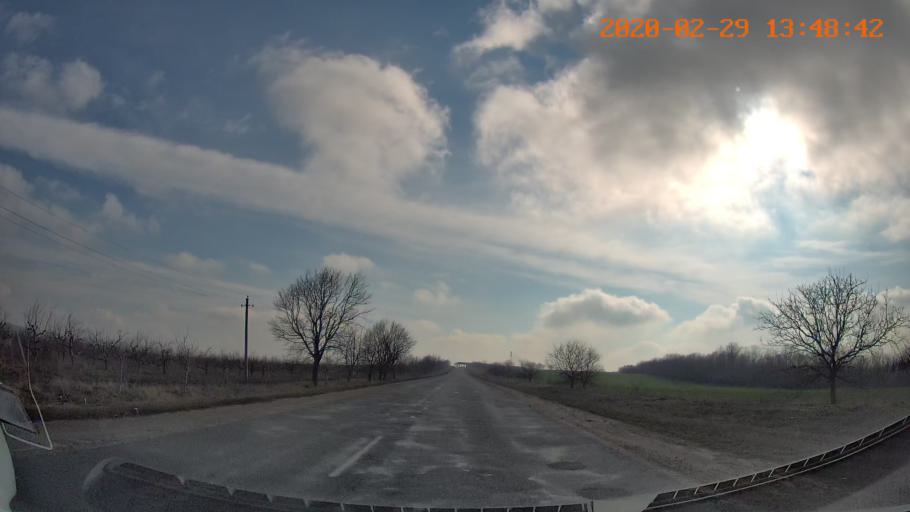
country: MD
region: Floresti
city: Leninskiy
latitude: 47.8512
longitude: 28.4871
